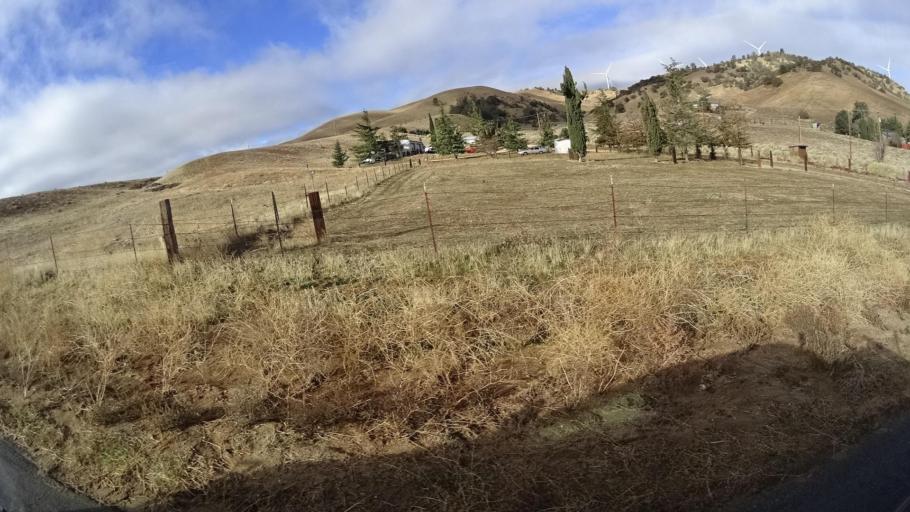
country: US
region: California
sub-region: Kern County
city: Tehachapi
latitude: 35.0723
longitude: -118.3423
